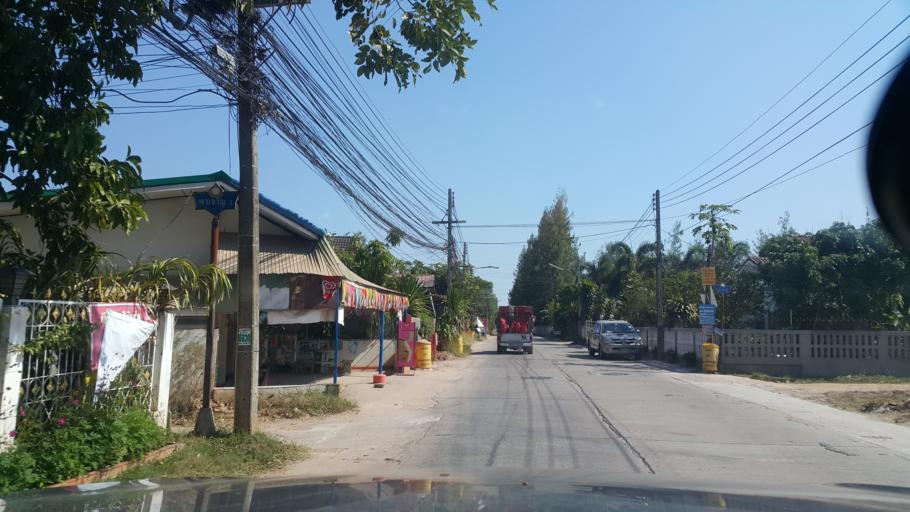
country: TH
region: Changwat Udon Thani
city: Udon Thani
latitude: 17.4550
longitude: 102.7810
